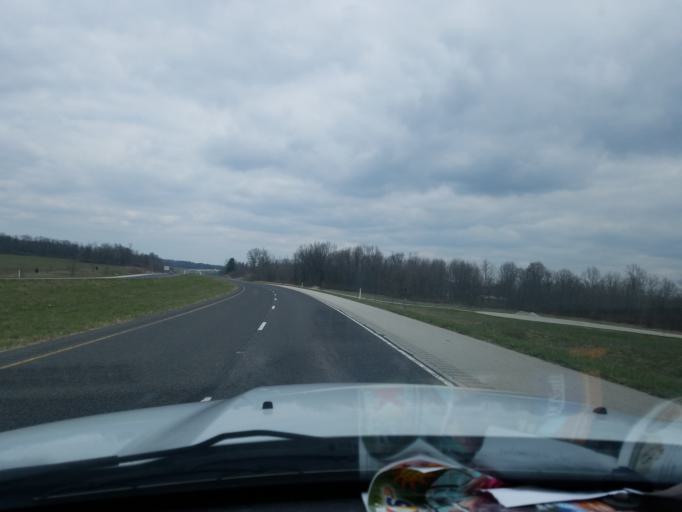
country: US
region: Indiana
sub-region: Vigo County
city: Terre Haute
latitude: 39.3806
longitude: -87.3732
